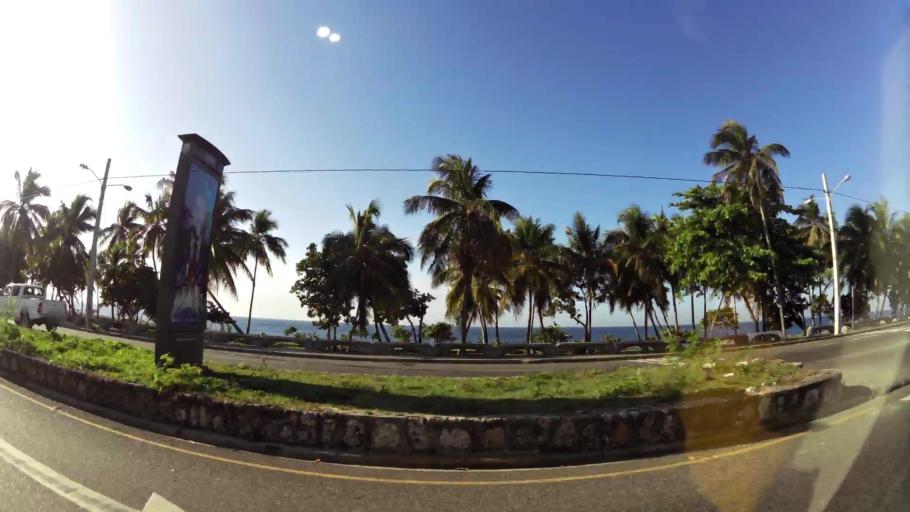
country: DO
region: Santo Domingo
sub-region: Santo Domingo
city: Santo Domingo Este
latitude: 18.4684
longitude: -69.8388
